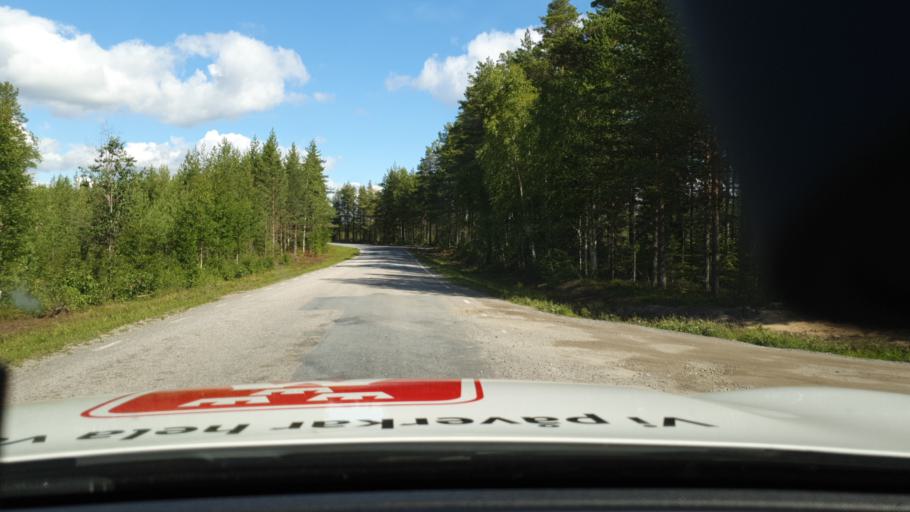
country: SE
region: Norrbotten
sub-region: Lulea Kommun
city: Ranea
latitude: 65.8010
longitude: 22.3080
